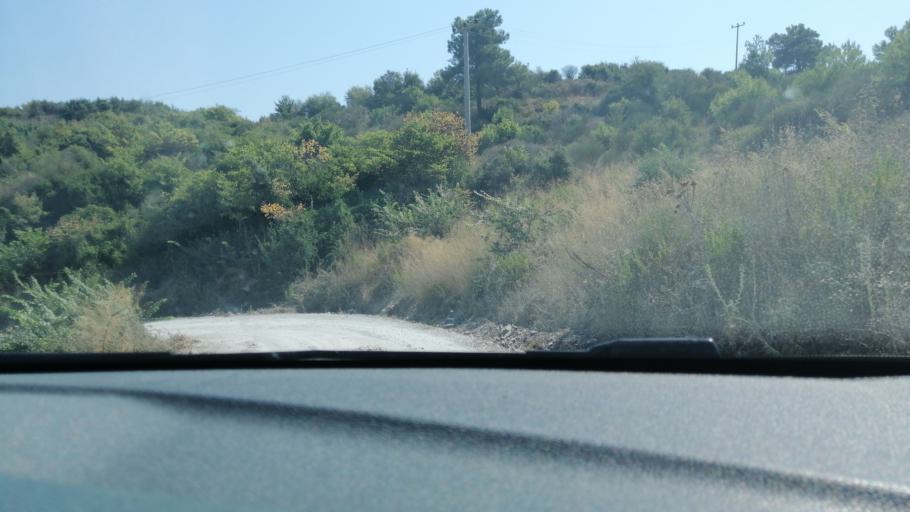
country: TR
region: Aydin
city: Davutlar
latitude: 37.7787
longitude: 27.3143
